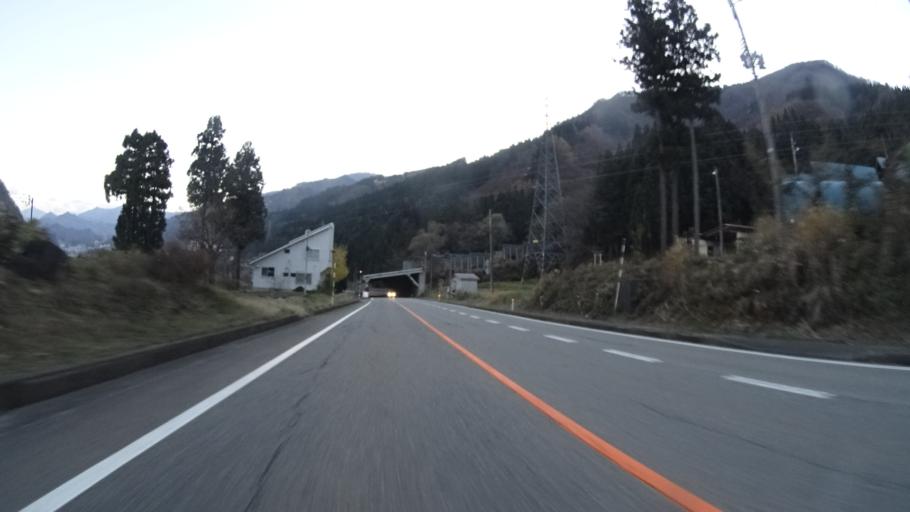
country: JP
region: Niigata
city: Shiozawa
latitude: 36.9610
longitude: 138.7997
